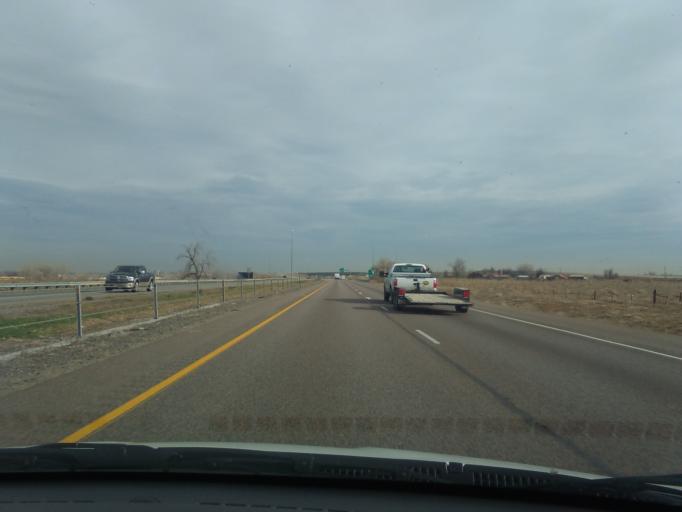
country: US
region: Colorado
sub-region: Adams County
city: Brighton
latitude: 39.9033
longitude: -104.8350
